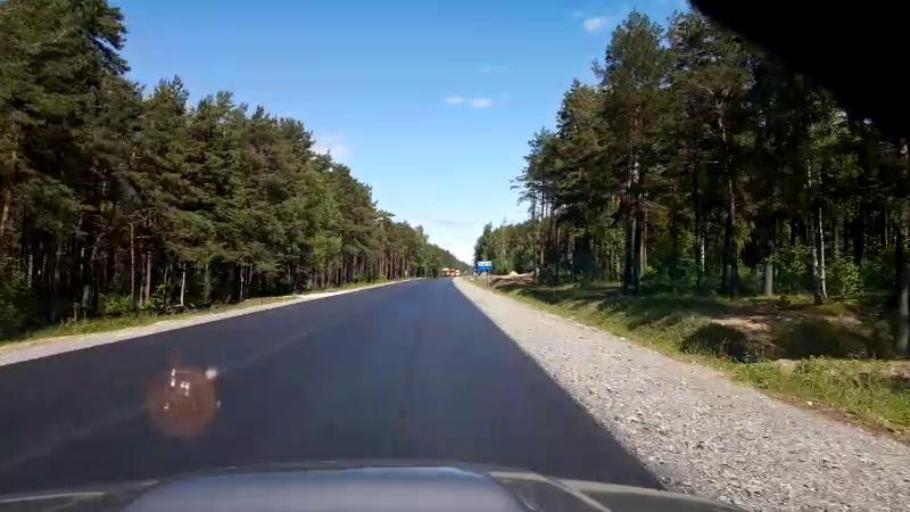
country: LV
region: Salacgrivas
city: Ainazi
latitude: 57.8389
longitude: 24.3473
